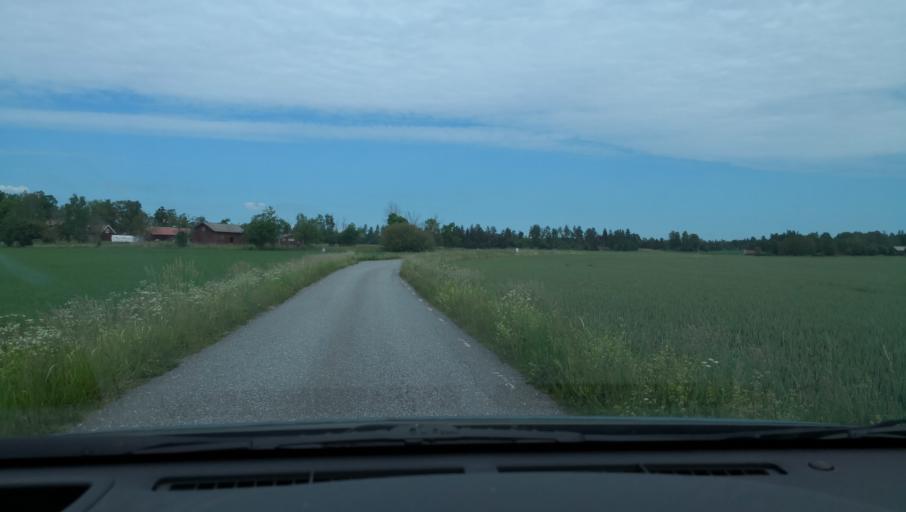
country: SE
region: Uppsala
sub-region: Enkopings Kommun
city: Orsundsbro
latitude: 59.7012
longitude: 17.4119
